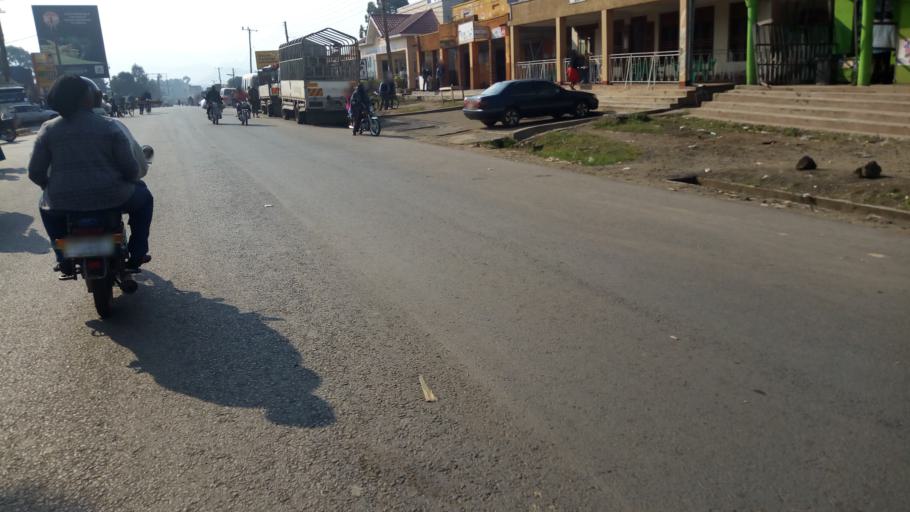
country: UG
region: Western Region
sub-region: Kisoro District
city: Kisoro
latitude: -1.2825
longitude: 29.6968
